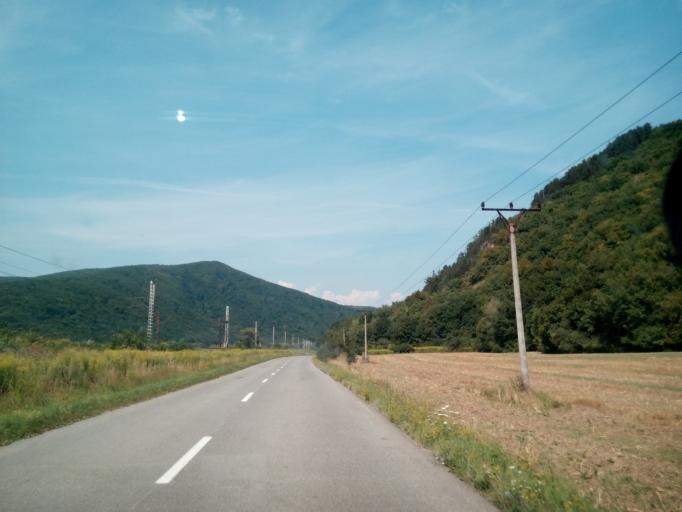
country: SK
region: Kosicky
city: Kosice
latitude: 48.8222
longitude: 21.2319
